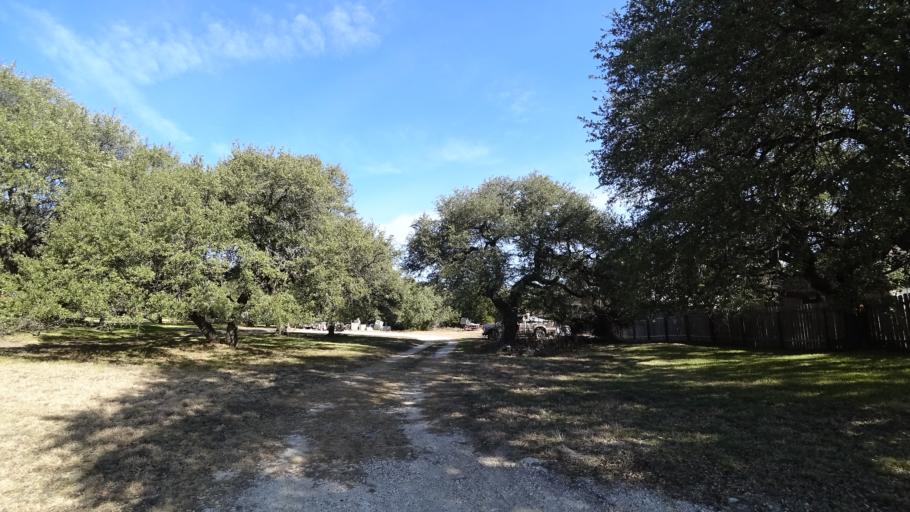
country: US
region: Texas
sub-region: Travis County
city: Wells Branch
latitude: 30.3948
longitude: -97.6972
